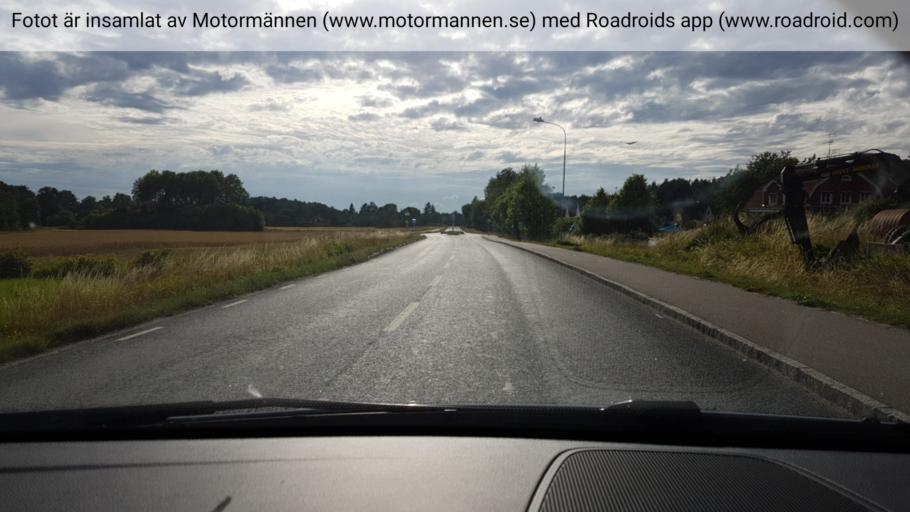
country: SE
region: Stockholm
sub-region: Norrtalje Kommun
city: Skanninge
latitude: 59.8947
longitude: 18.4853
